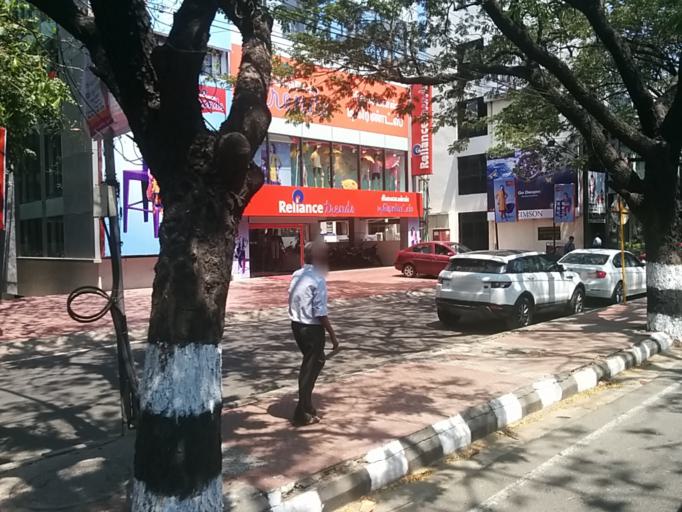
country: IN
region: Tamil Nadu
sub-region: Chennai
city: Gandhi Nagar
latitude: 13.0069
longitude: 80.2508
